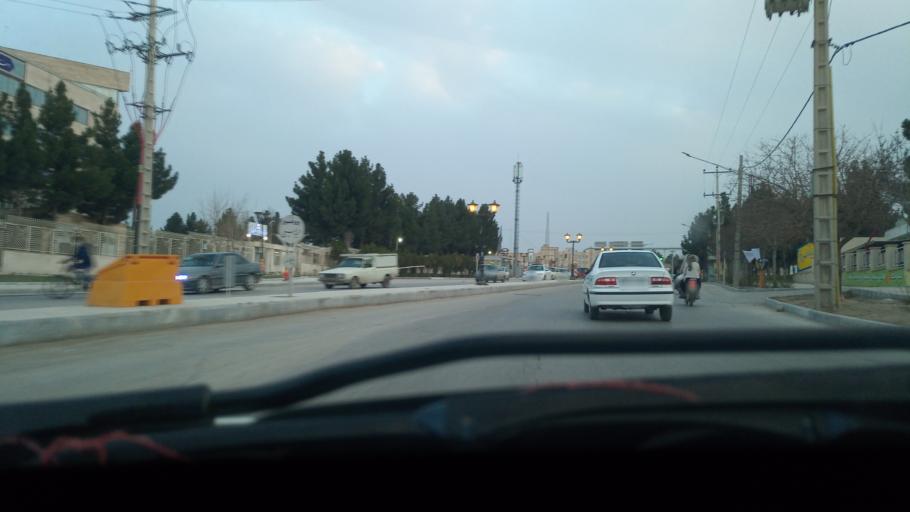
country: IR
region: Khorasan-e Shomali
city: Bojnurd
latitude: 37.4617
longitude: 57.3326
